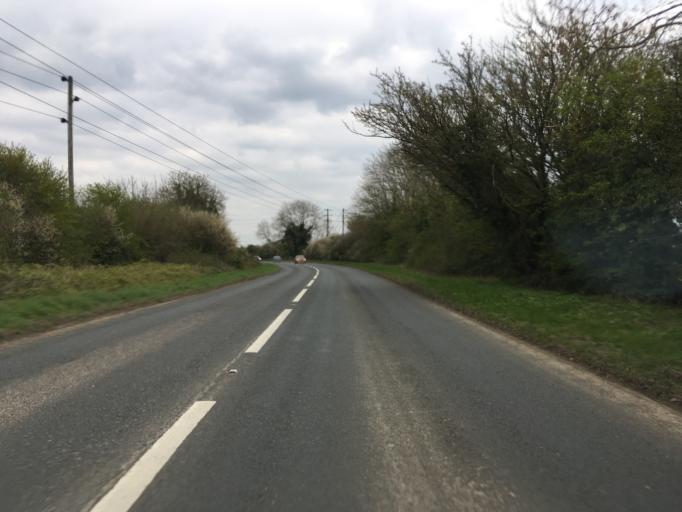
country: GB
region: England
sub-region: Gloucestershire
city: Cirencester
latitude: 51.7273
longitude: -1.9281
